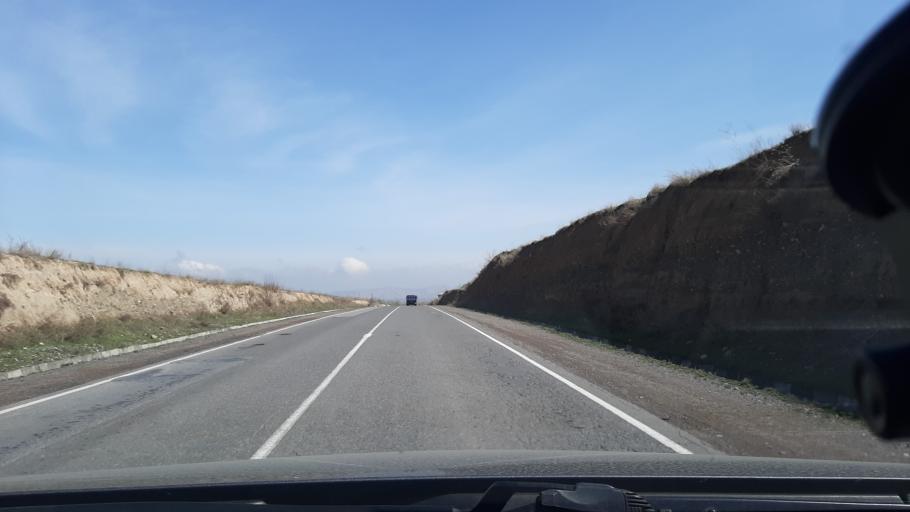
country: TJ
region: Viloyati Sughd
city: Shahriston
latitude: 39.7683
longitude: 68.8217
